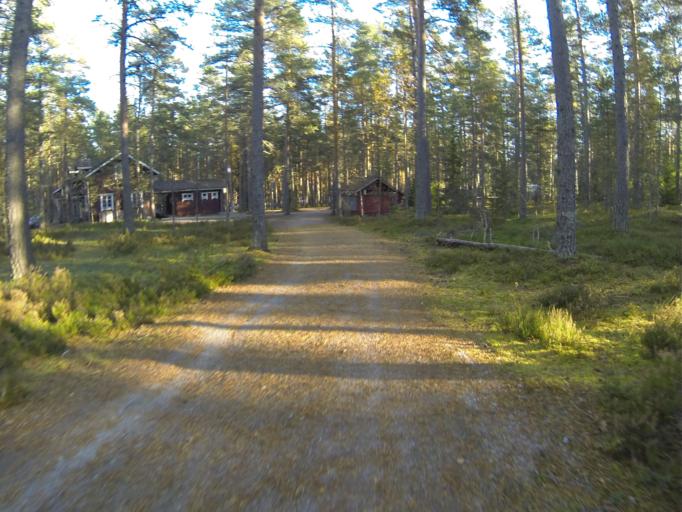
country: FI
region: Varsinais-Suomi
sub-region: Salo
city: Saerkisalo
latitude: 60.2102
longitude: 22.9353
